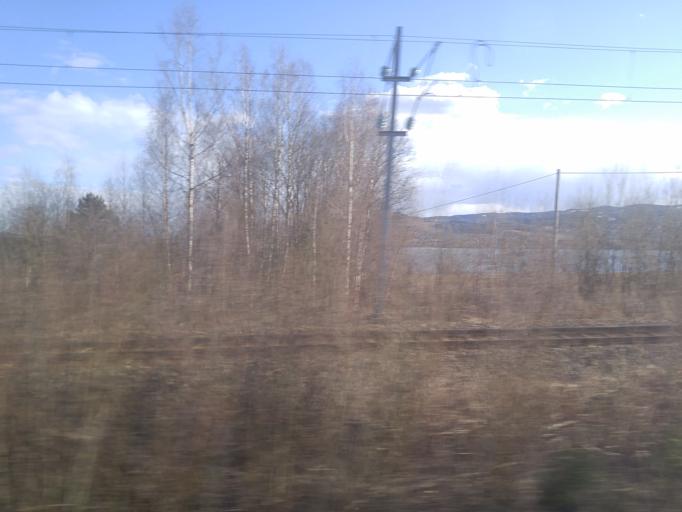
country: NO
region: Hedmark
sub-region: Ringsaker
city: Moelv
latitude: 60.9823
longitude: 10.6360
